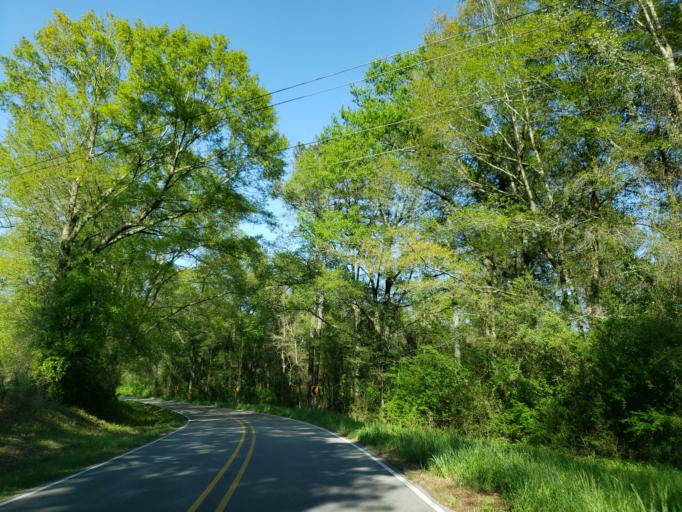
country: US
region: Mississippi
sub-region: Jones County
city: Ellisville
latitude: 31.5952
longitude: -89.3776
